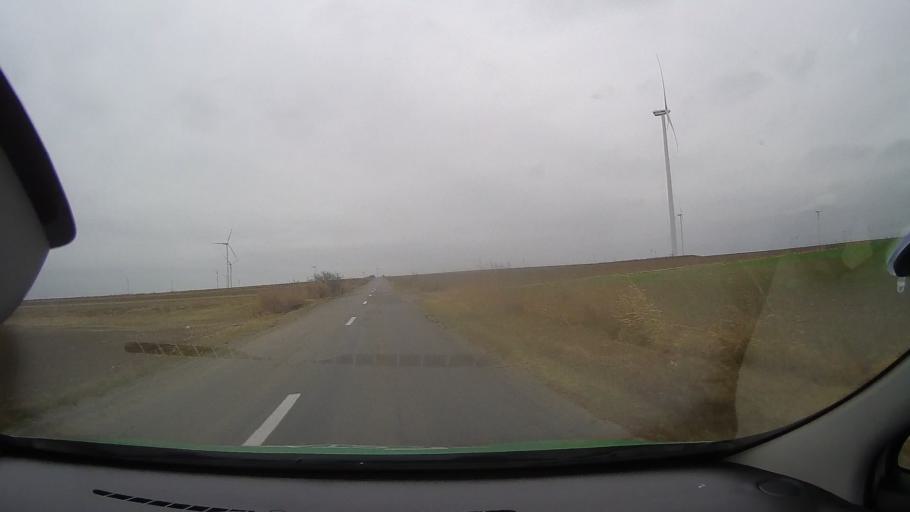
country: RO
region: Constanta
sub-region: Comuna Pantelimon
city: Pantelimon
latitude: 44.5057
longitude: 28.3465
